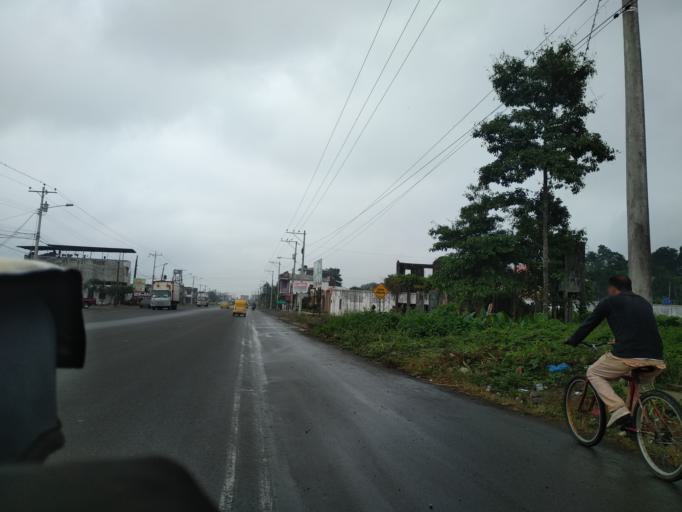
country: EC
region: Cotopaxi
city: La Mana
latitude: -0.9489
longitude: -79.3426
